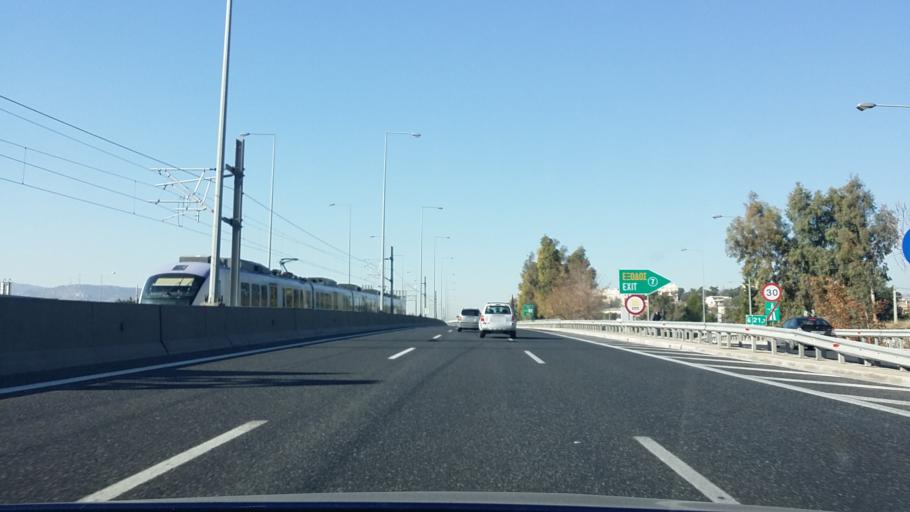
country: GR
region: Attica
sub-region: Nomarchia Anatolikis Attikis
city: Acharnes
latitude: 38.0663
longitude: 23.7356
